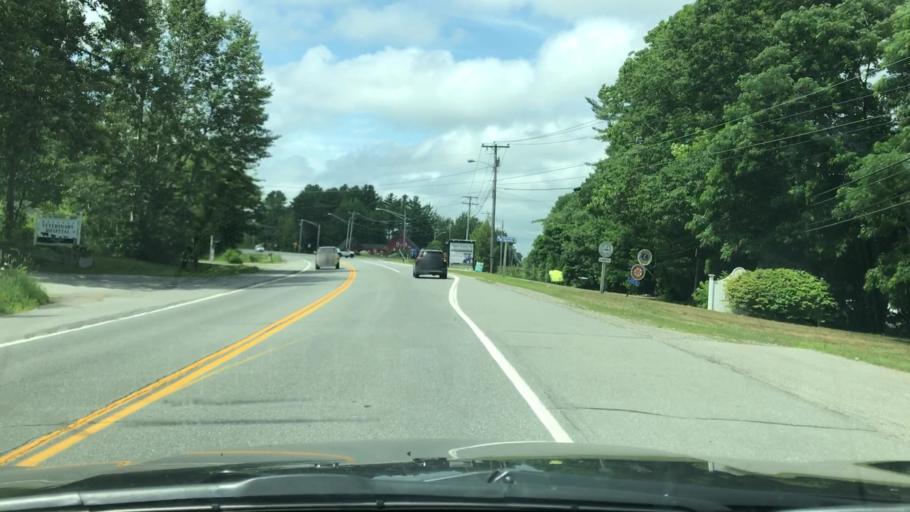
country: US
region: Maine
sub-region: Waldo County
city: Belfast
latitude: 44.4070
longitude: -68.9918
